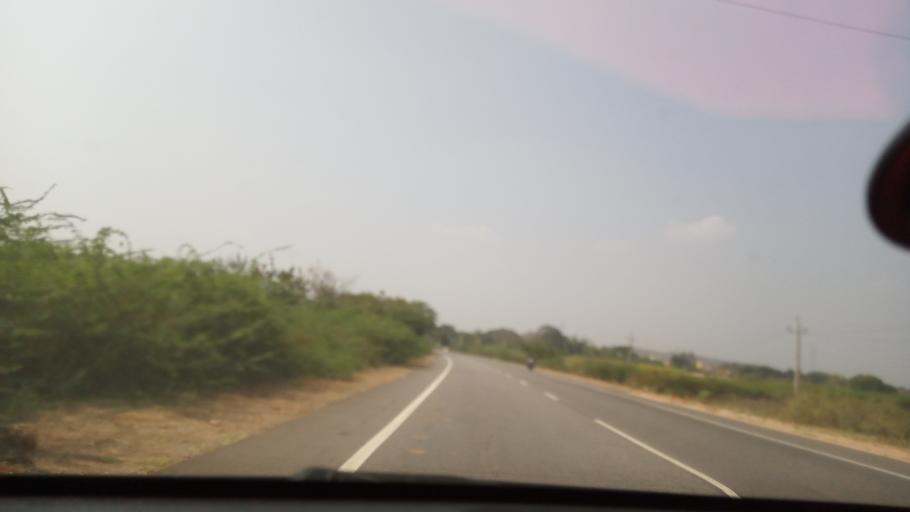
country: IN
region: Karnataka
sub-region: Mysore
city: Nanjangud
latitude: 12.0810
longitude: 76.7356
